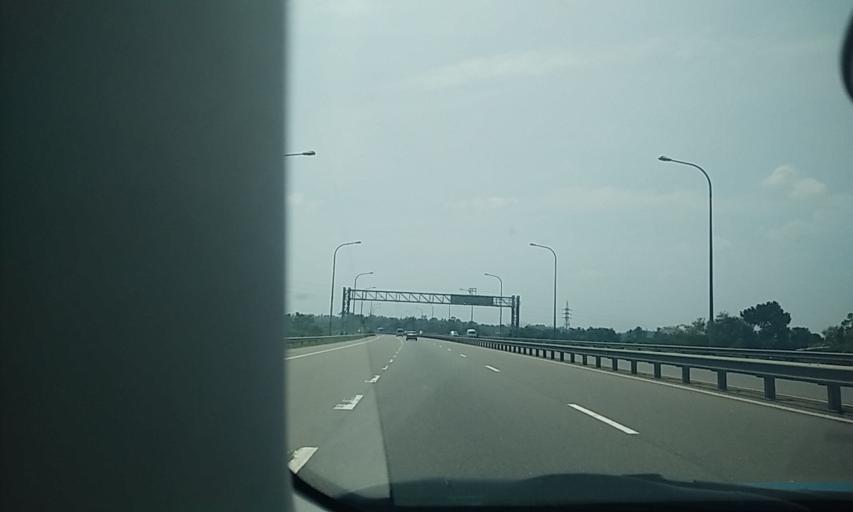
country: LK
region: Western
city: Homagama
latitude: 6.7795
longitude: 79.9802
